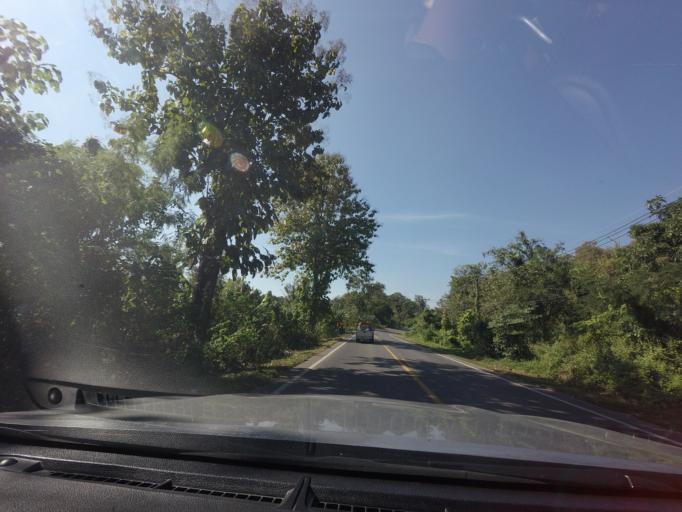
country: TH
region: Sukhothai
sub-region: Amphoe Si Satchanalai
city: Si Satchanalai
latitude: 17.6076
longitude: 99.7082
